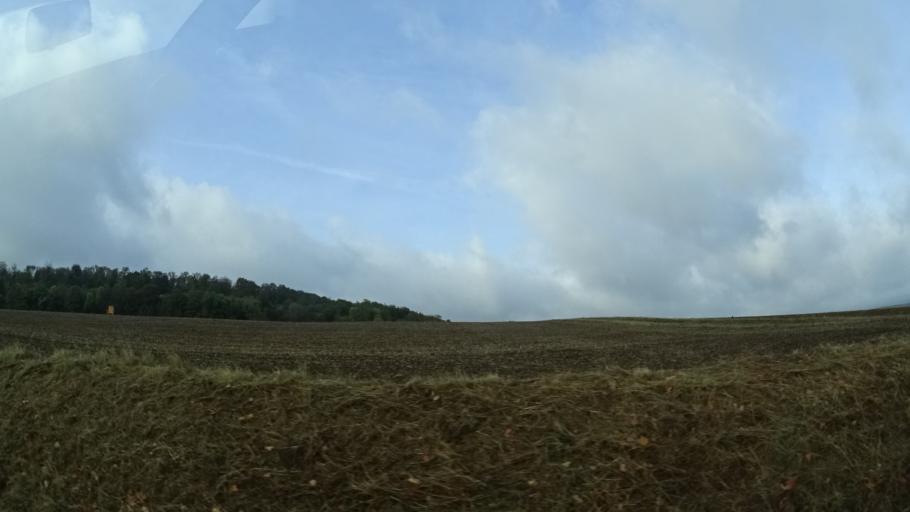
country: DE
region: Hesse
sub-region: Regierungsbezirk Giessen
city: Freiensteinau
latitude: 50.4708
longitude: 9.4071
